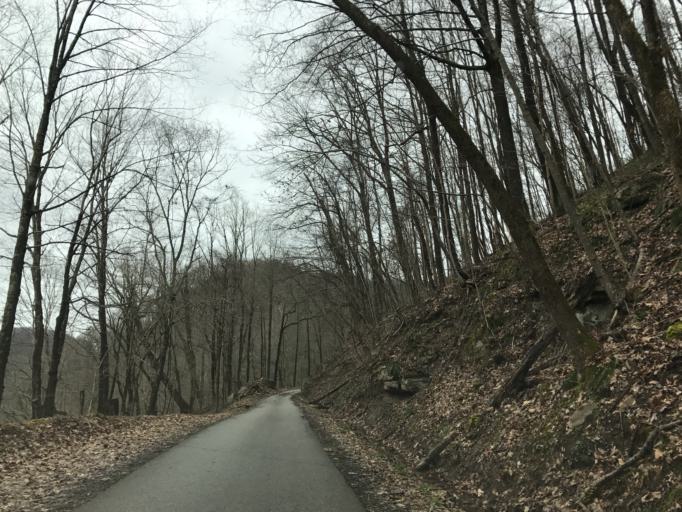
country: US
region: West Virginia
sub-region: Fayette County
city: Fayetteville
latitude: 38.0666
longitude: -81.0830
